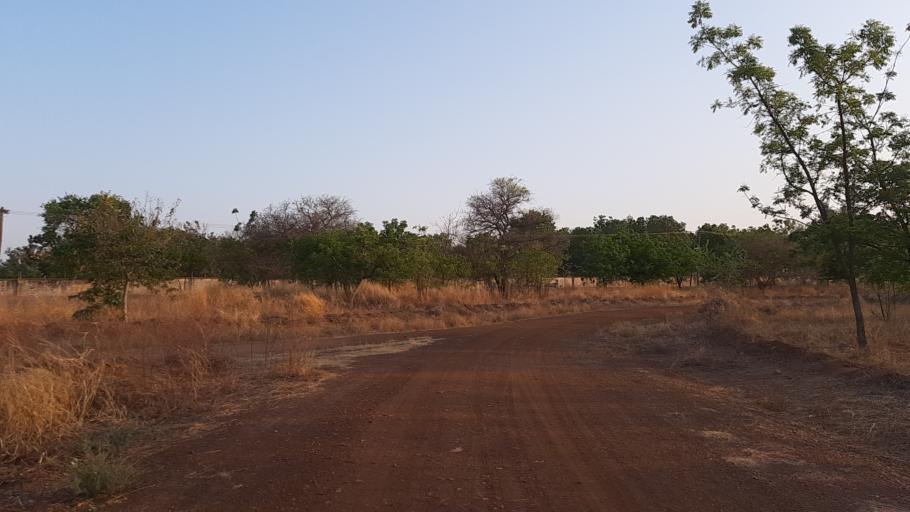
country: GH
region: Upper East
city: Bolgatanga
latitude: 10.6725
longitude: -0.8650
